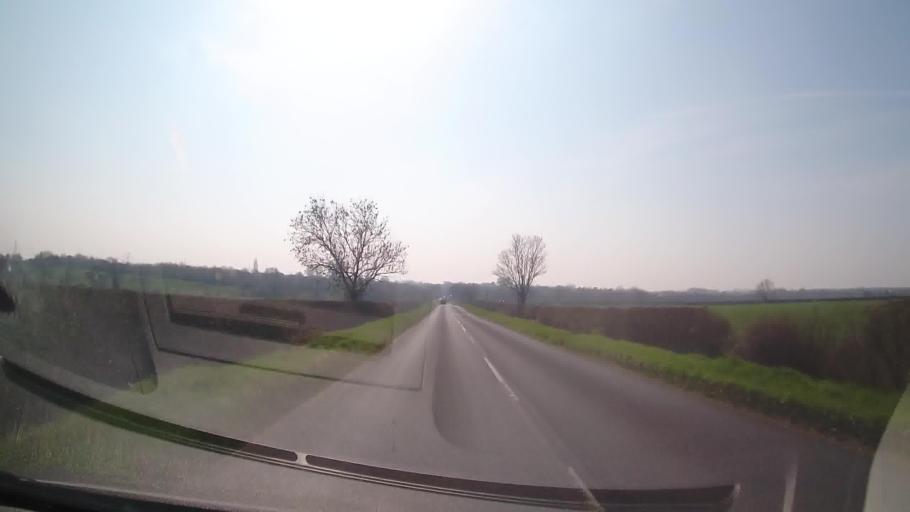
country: GB
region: England
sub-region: Leicestershire
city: Anstey
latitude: 52.6654
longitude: -1.2064
